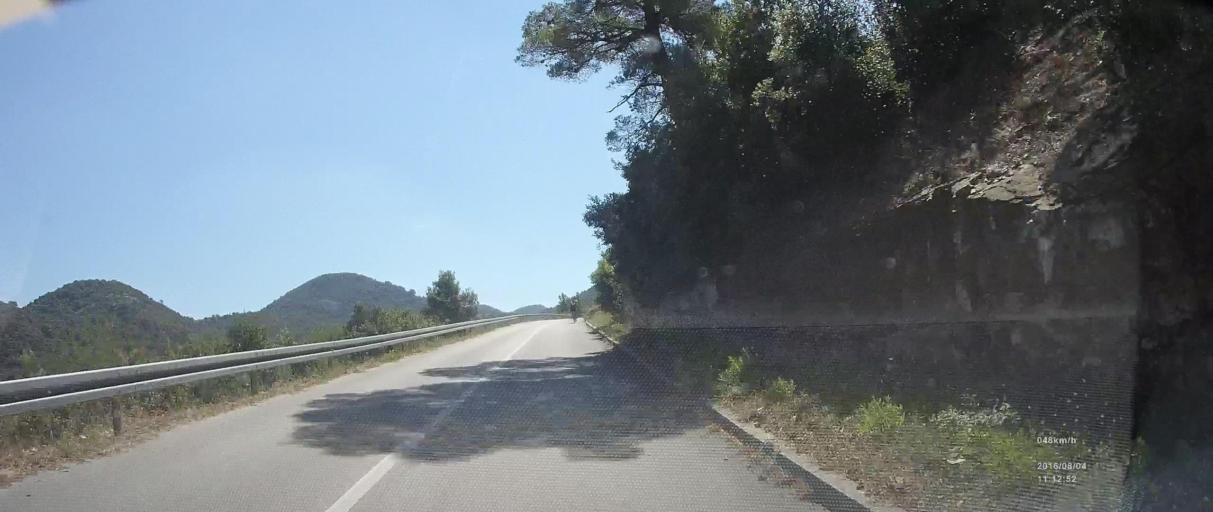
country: HR
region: Dubrovacko-Neretvanska
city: Blato
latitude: 42.7572
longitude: 17.4778
